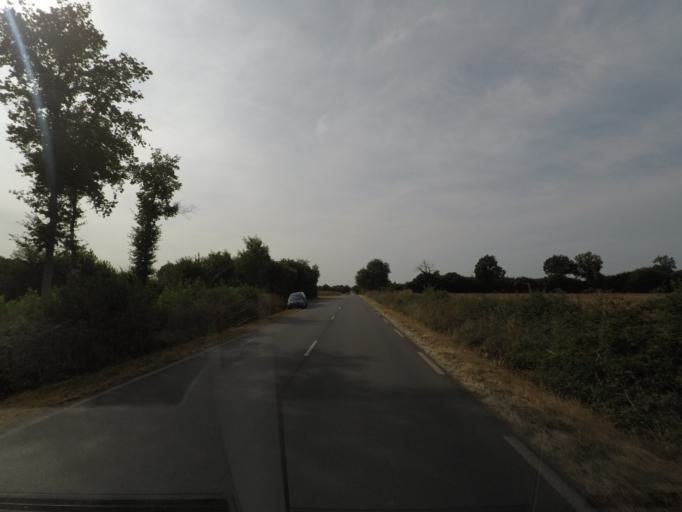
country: FR
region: Poitou-Charentes
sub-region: Departement des Deux-Sevres
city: Lezay
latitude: 46.1728
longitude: -0.0022
